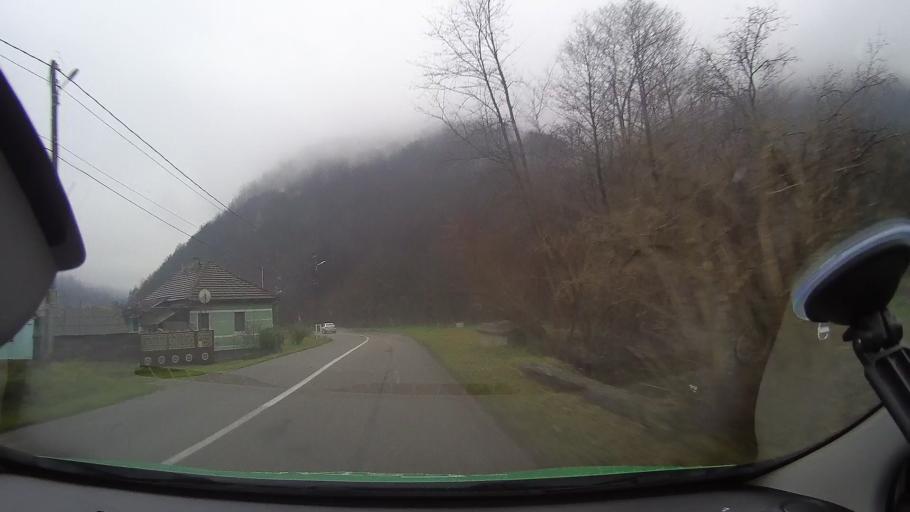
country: RO
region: Arad
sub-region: Comuna Dezna
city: Dezna
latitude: 46.4212
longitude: 22.2575
